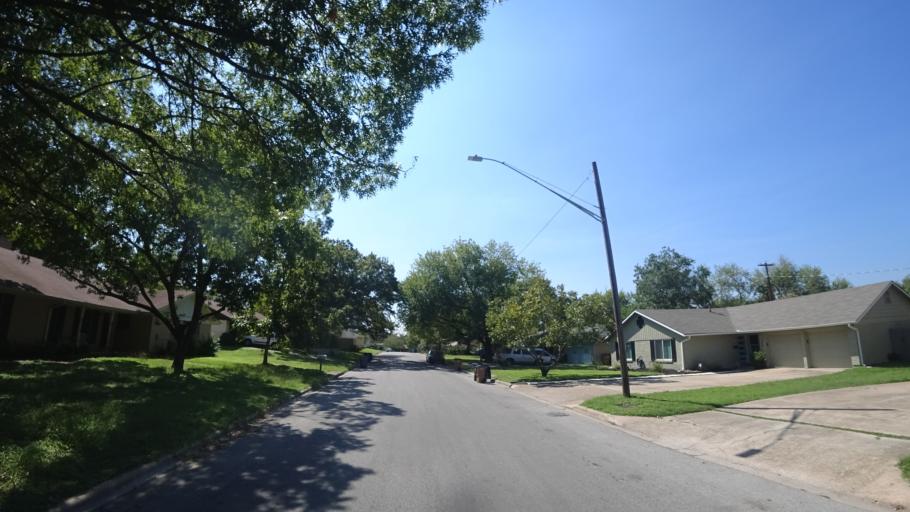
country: US
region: Texas
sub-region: Travis County
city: Austin
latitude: 30.3105
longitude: -97.6859
